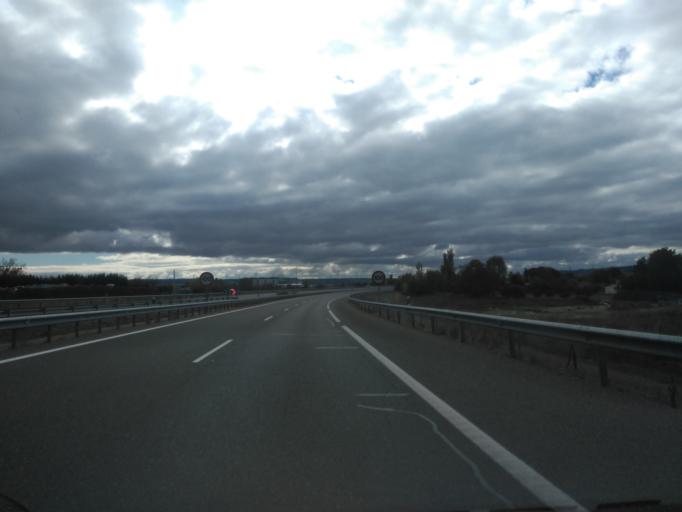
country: ES
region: Castille and Leon
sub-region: Provincia de Palencia
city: Villamuriel de Cerrato
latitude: 41.9754
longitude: -4.5008
